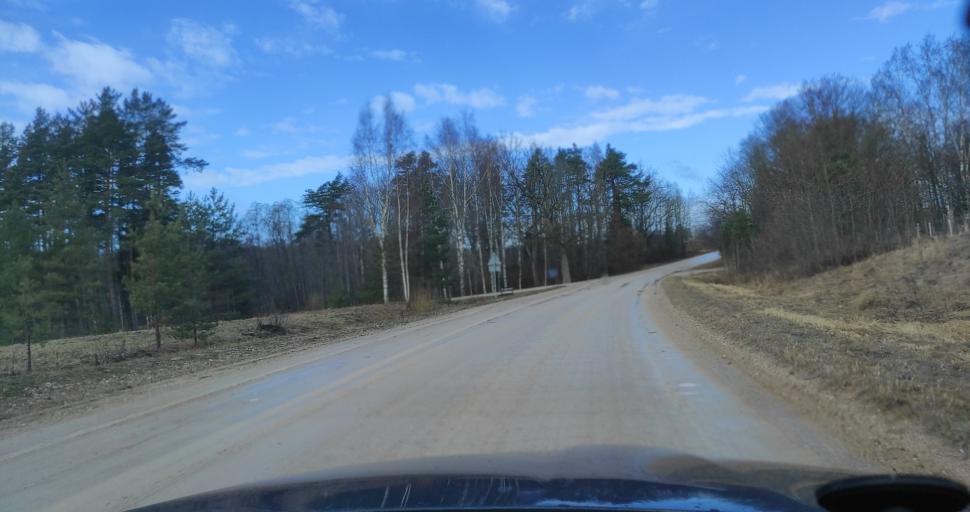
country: LV
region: Tukuma Rajons
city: Tukums
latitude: 57.1096
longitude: 23.0300
